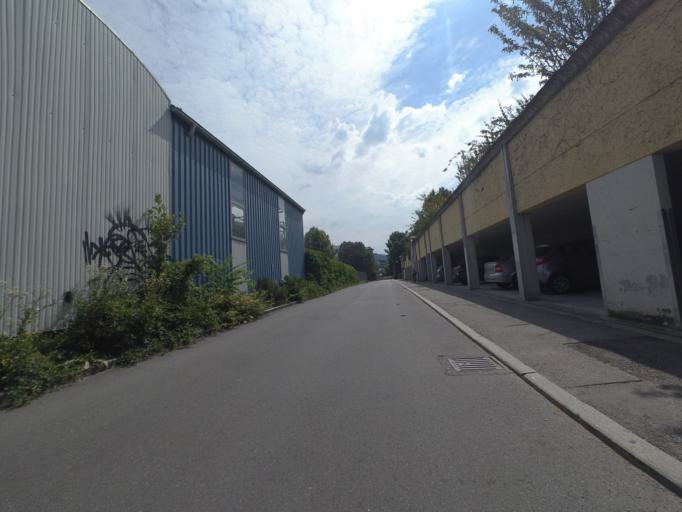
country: AT
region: Salzburg
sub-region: Salzburg Stadt
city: Salzburg
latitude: 47.8078
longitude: 13.0228
